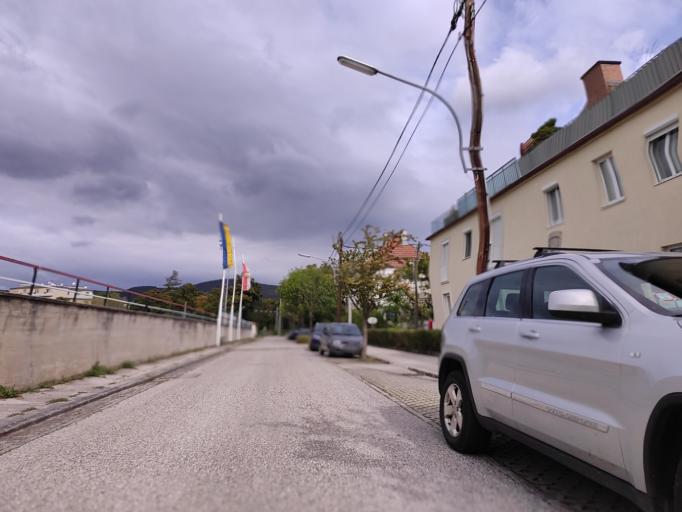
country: AT
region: Lower Austria
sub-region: Politischer Bezirk Baden
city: Baden
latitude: 48.0045
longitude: 16.2472
